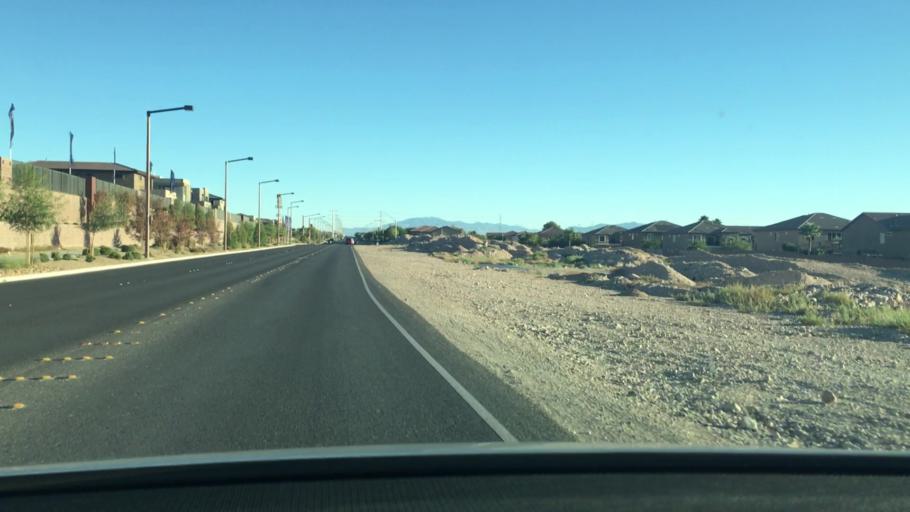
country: US
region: Nevada
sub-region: Clark County
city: Summerlin South
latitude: 36.0749
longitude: -115.3157
